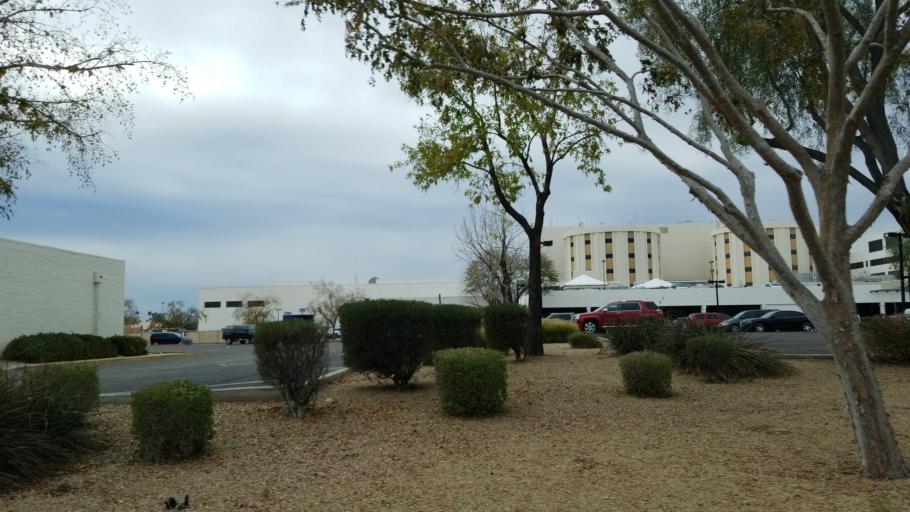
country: US
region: Arizona
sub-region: Maricopa County
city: Sun City
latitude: 33.6034
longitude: -112.2813
